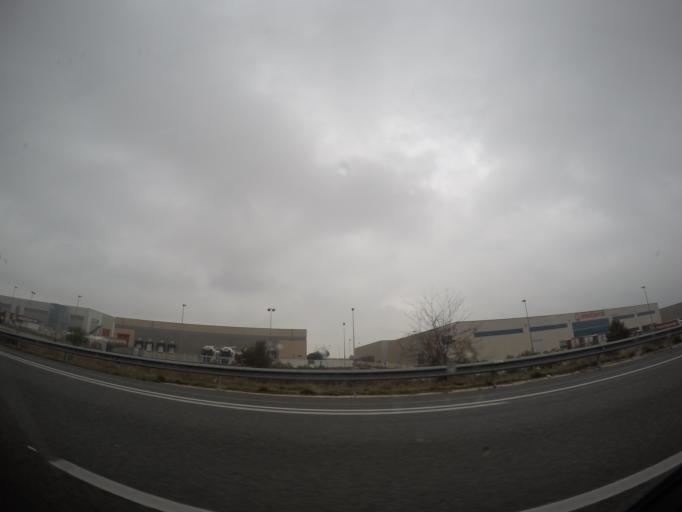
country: ES
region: Catalonia
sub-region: Provincia de Barcelona
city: Vilafranca del Penedes
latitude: 41.3293
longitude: 1.6744
